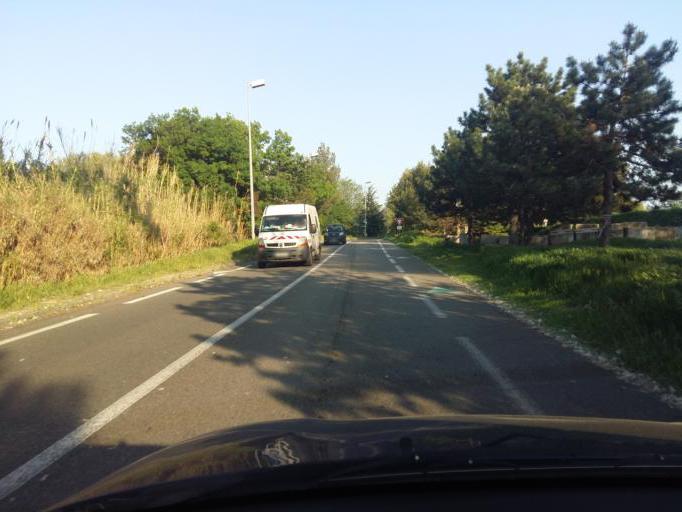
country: FR
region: Provence-Alpes-Cote d'Azur
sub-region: Departement du Vaucluse
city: Avignon
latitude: 43.9533
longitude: 4.7956
